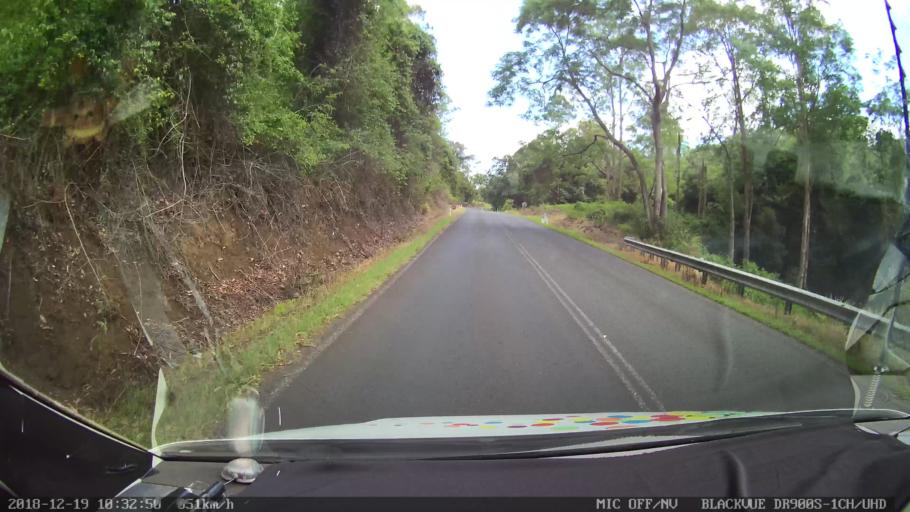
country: AU
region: New South Wales
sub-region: Lismore Municipality
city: Larnook
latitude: -28.5794
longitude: 153.1240
